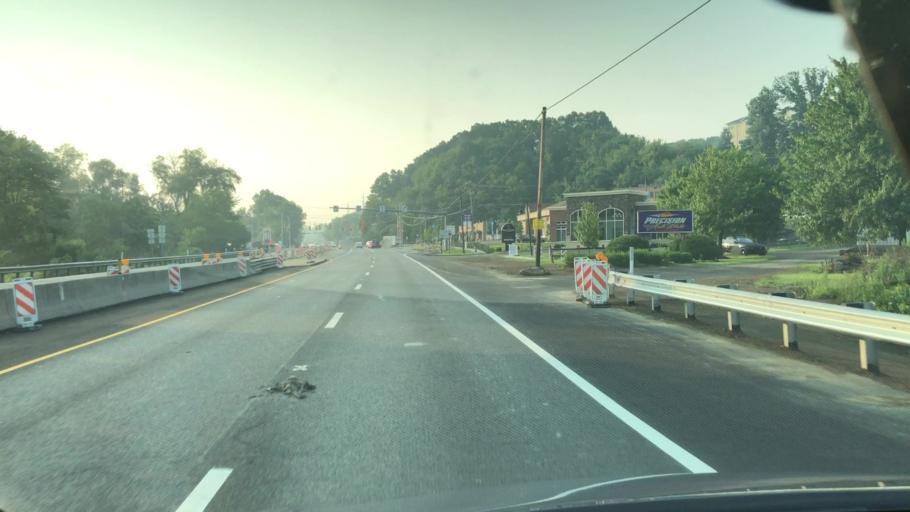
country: US
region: Pennsylvania
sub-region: Allegheny County
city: Bradford Woods
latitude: 40.6566
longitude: -80.0891
